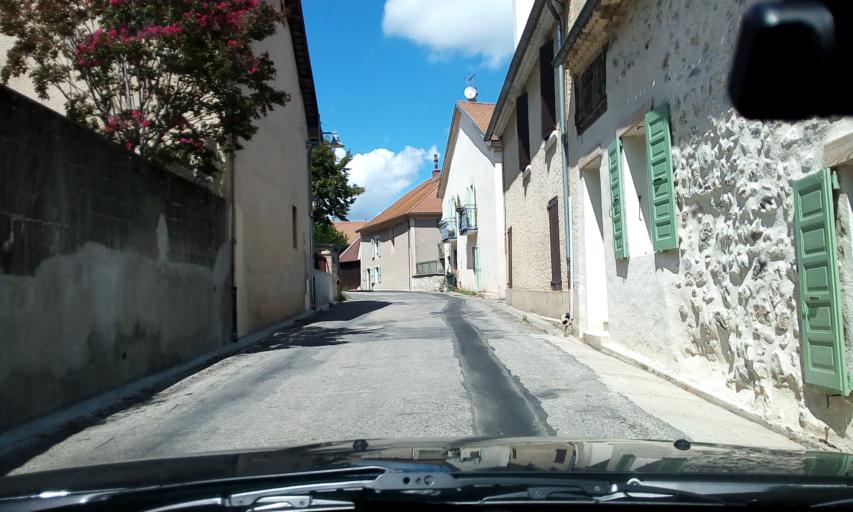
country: FR
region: Rhone-Alpes
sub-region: Departement de l'Isere
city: Mens
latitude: 44.7942
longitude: 5.6596
